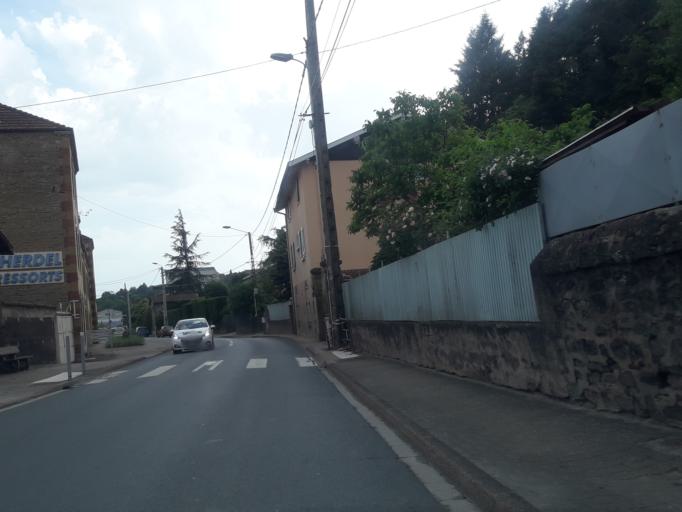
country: FR
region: Rhone-Alpes
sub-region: Departement du Rhone
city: Sain-Bel
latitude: 45.8295
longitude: 4.6099
